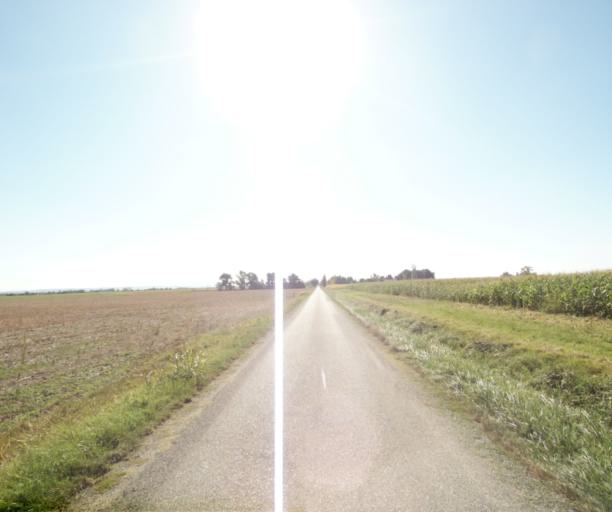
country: FR
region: Midi-Pyrenees
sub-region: Departement du Tarn-et-Garonne
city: Verdun-sur-Garonne
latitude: 43.8410
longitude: 1.2096
